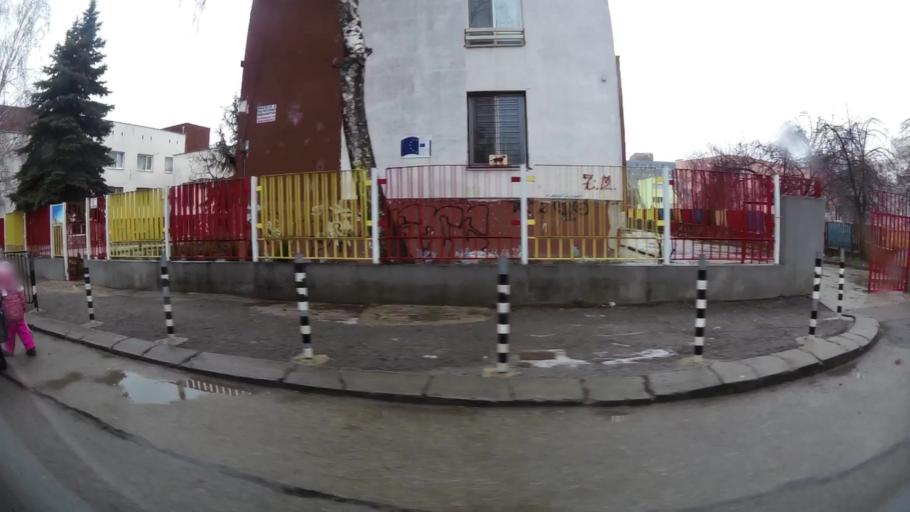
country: BG
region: Sofia-Capital
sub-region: Stolichna Obshtina
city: Sofia
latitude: 42.6293
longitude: 23.3791
